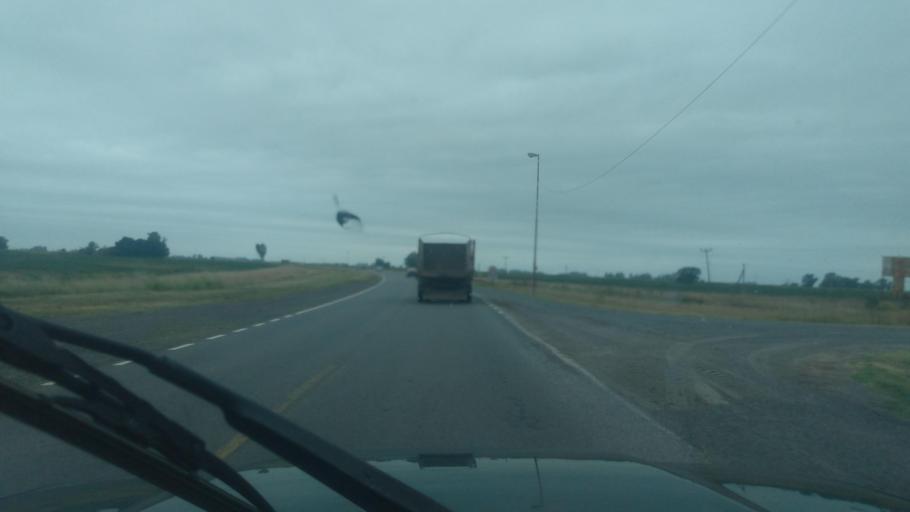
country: AR
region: Buenos Aires
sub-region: Partido de Nueve de Julio
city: Nueve de Julio
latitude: -35.3969
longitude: -60.7460
